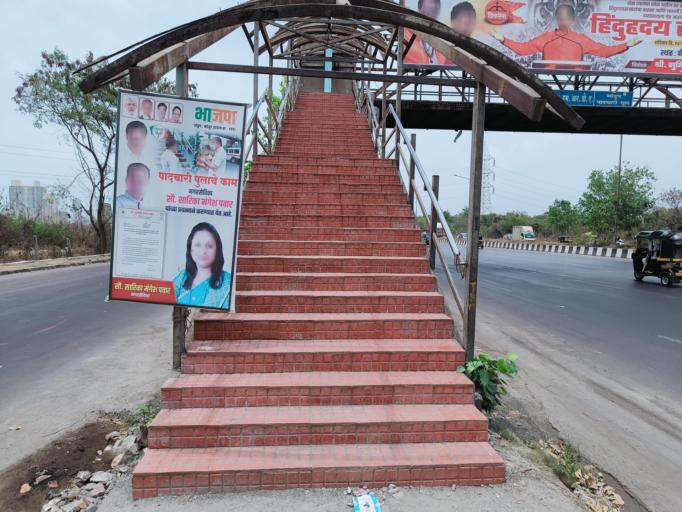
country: IN
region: Maharashtra
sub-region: Thane
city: Airoli
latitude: 19.1455
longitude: 72.9485
